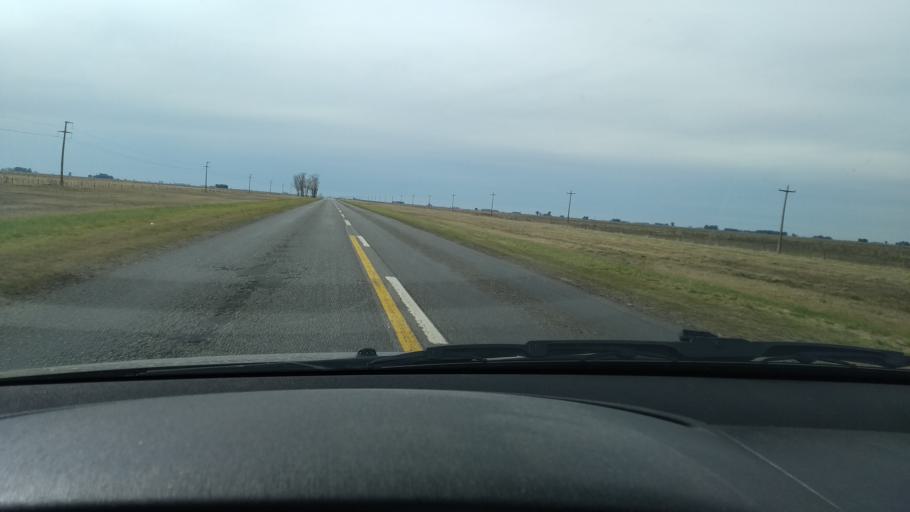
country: AR
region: Buenos Aires
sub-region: Partido de Azul
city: Azul
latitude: -36.7062
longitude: -59.7569
